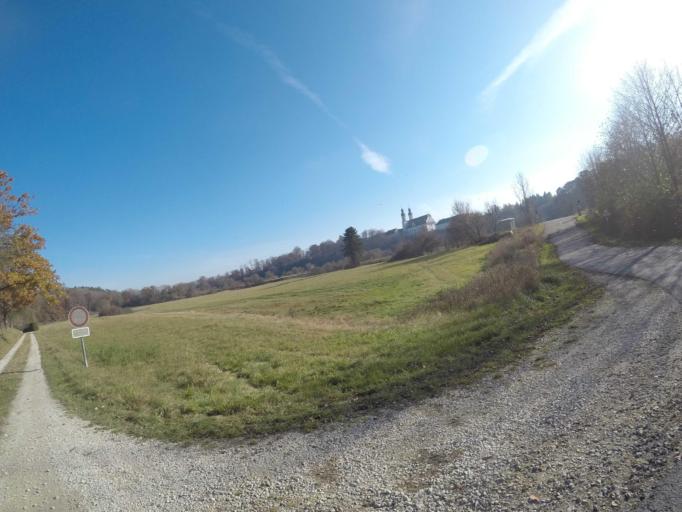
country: DE
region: Baden-Wuerttemberg
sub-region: Tuebingen Region
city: Obermarchtal
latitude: 48.2401
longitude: 9.5642
